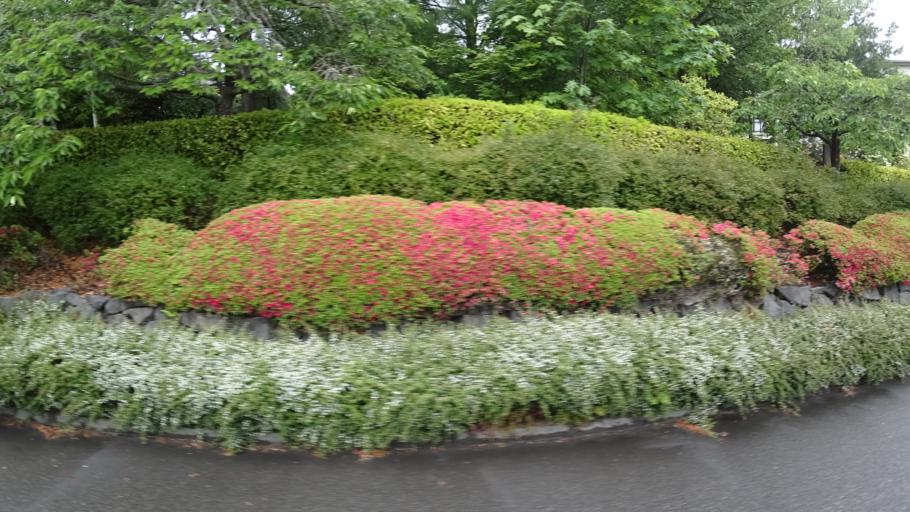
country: US
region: Oregon
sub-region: Washington County
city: West Haven
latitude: 45.5344
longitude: -122.7661
